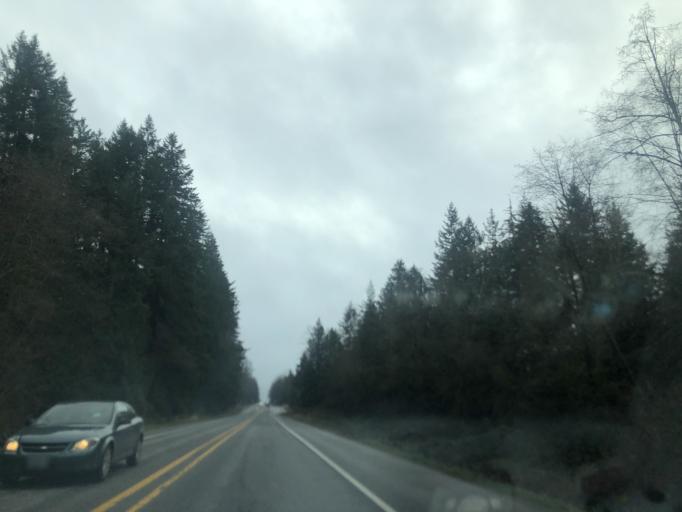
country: US
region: Washington
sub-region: Snohomish County
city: Sisco Heights
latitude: 48.0952
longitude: -122.1119
